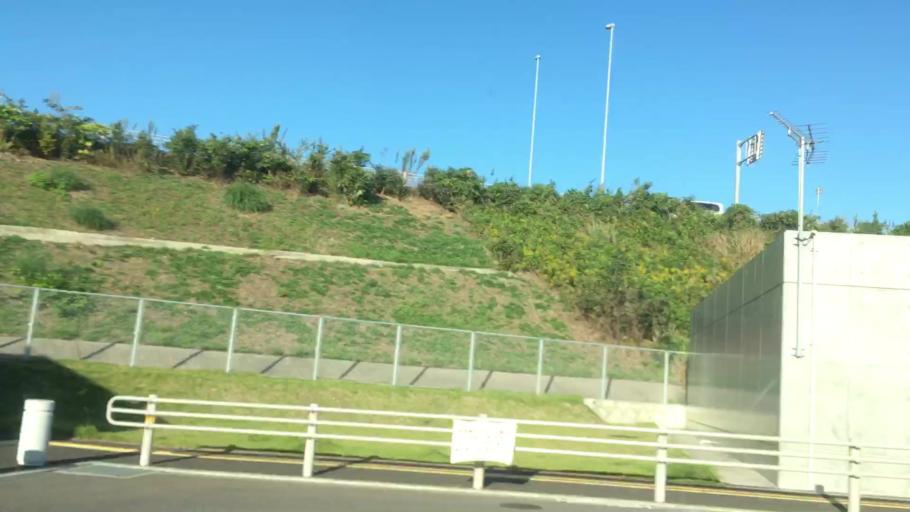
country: JP
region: Nagasaki
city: Sasebo
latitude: 33.2012
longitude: 129.6723
